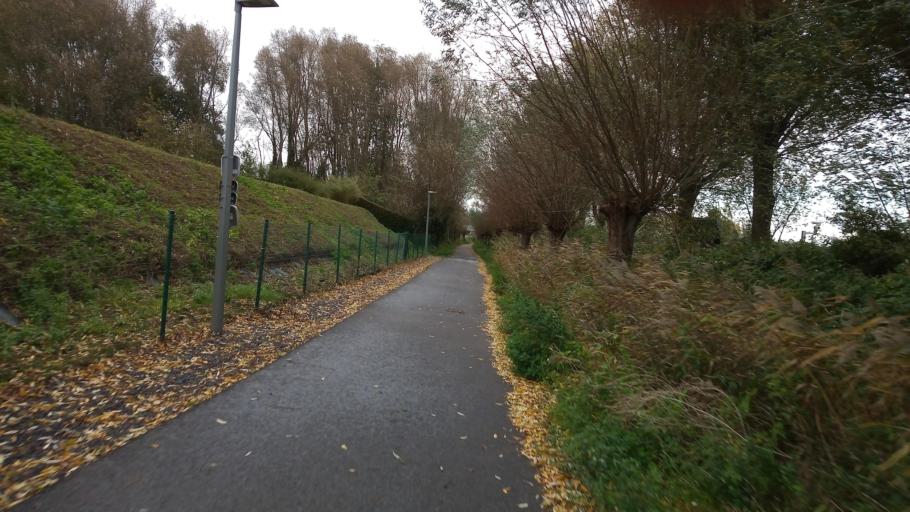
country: BE
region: Flanders
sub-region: Provincie West-Vlaanderen
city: Kortrijk
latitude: 50.8239
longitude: 3.2377
